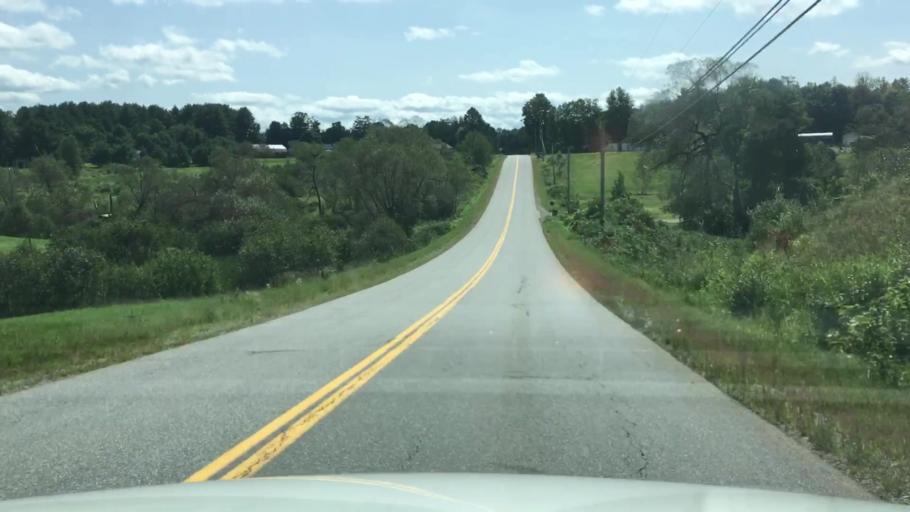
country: US
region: Maine
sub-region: Kennebec County
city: Augusta
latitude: 44.3493
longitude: -69.8121
